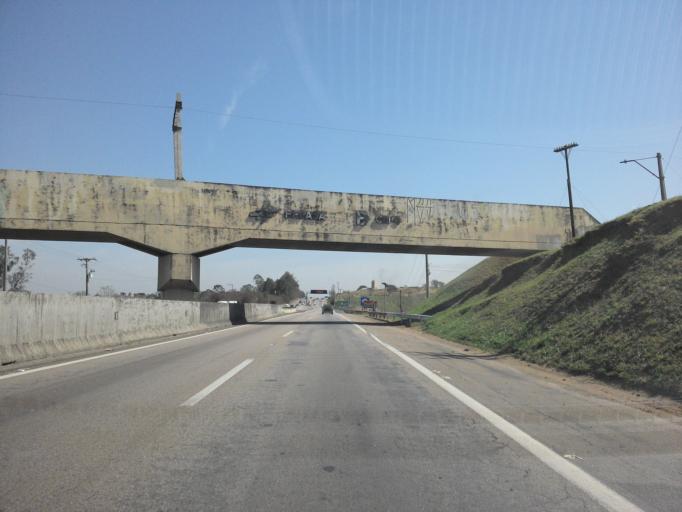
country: BR
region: Sao Paulo
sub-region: Campinas
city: Campinas
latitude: -22.8922
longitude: -47.1359
